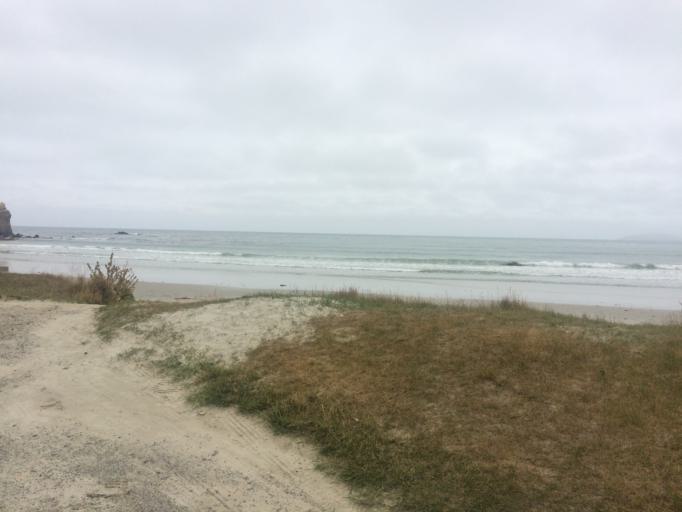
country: NZ
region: Otago
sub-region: Dunedin City
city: Portobello
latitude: -45.6423
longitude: 170.6618
